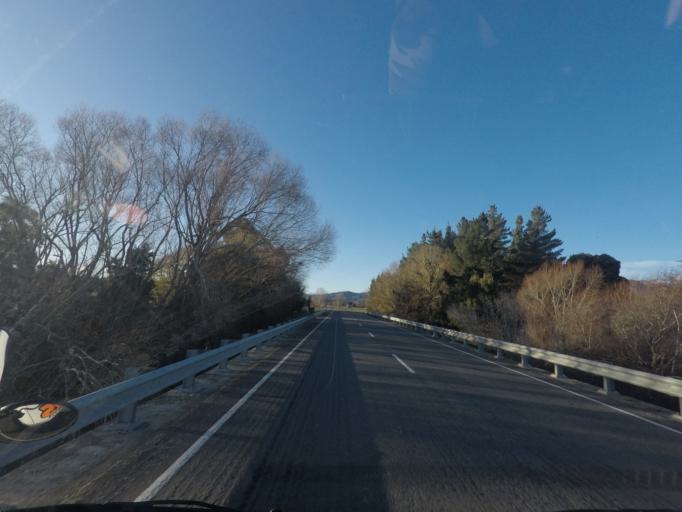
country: NZ
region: Canterbury
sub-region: Kaikoura District
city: Kaikoura
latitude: -42.7199
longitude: 173.2856
